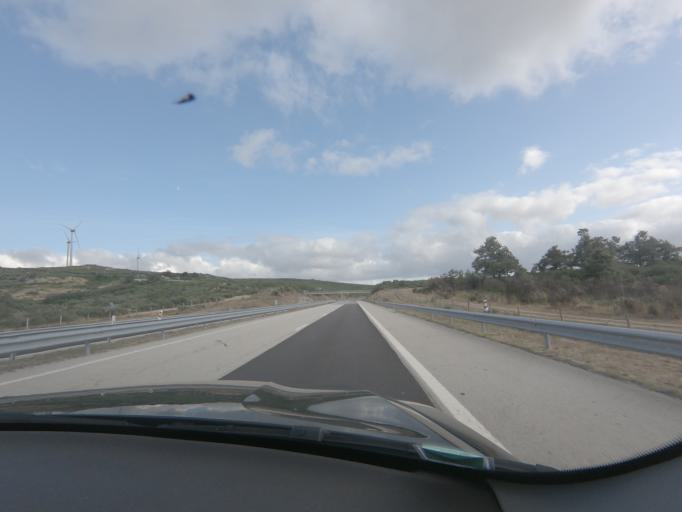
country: PT
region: Viseu
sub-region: Tarouca
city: Tarouca
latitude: 40.9990
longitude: -7.8829
